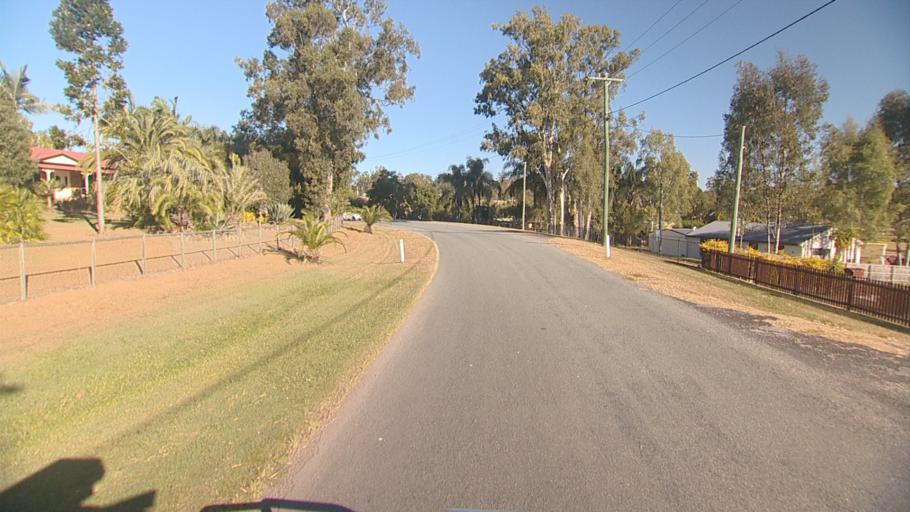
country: AU
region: Queensland
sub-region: Logan
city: North Maclean
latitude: -27.7903
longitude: 153.0243
